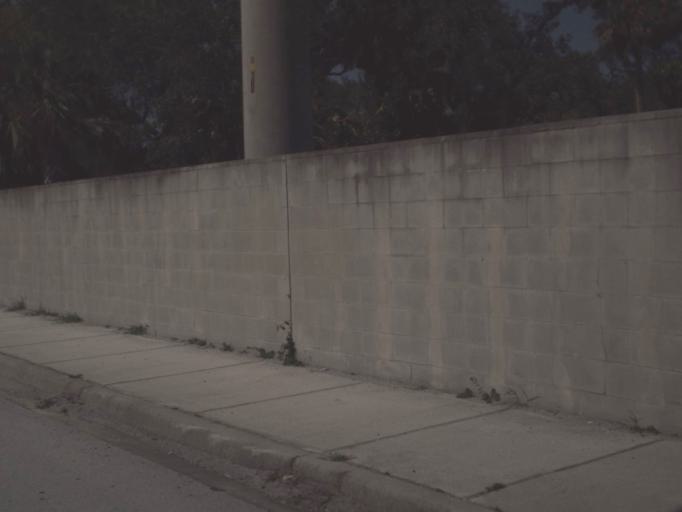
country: US
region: Florida
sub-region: Brevard County
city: South Patrick Shores
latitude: 28.1635
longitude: -80.6429
